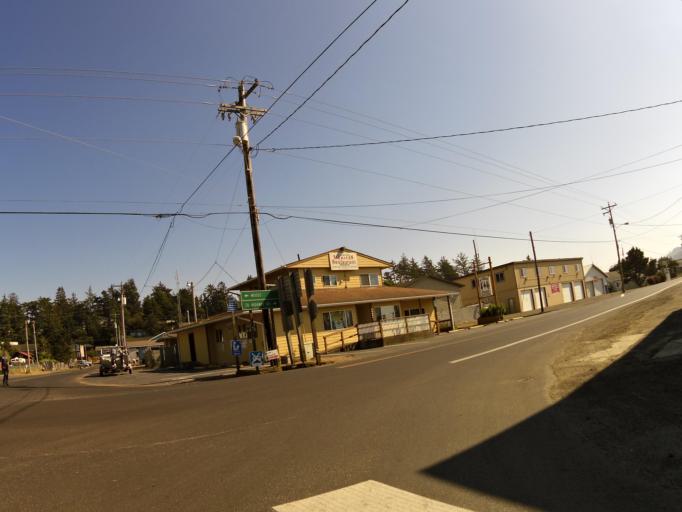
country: US
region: Oregon
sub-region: Tillamook County
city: Pacific City
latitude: 45.2017
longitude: -123.9619
